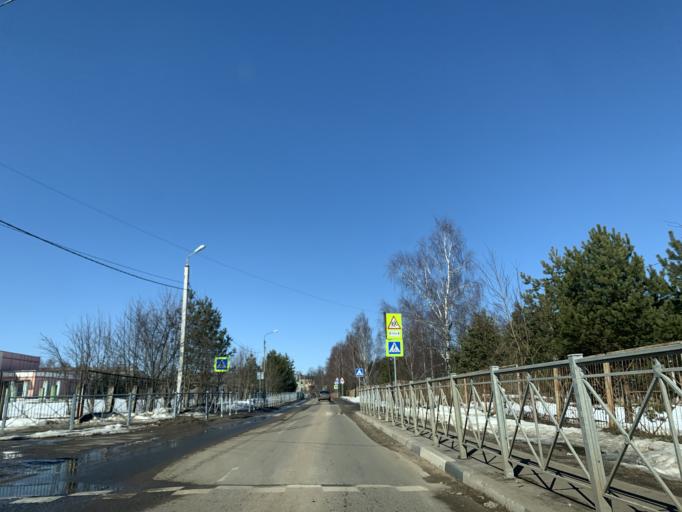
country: RU
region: Jaroslavl
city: Konstantinovskiy
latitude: 57.8390
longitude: 39.5826
